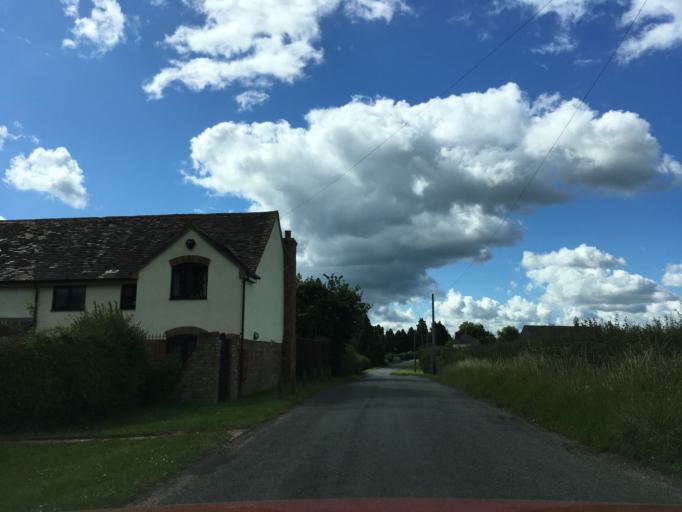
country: GB
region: England
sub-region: Gloucestershire
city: Newent
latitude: 51.8564
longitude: -2.3528
